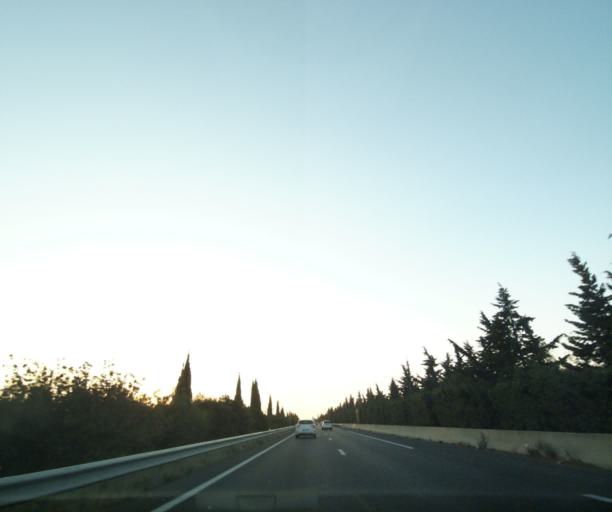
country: FR
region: Provence-Alpes-Cote d'Azur
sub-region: Departement des Bouches-du-Rhone
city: Mouries
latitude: 43.6389
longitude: 4.9060
